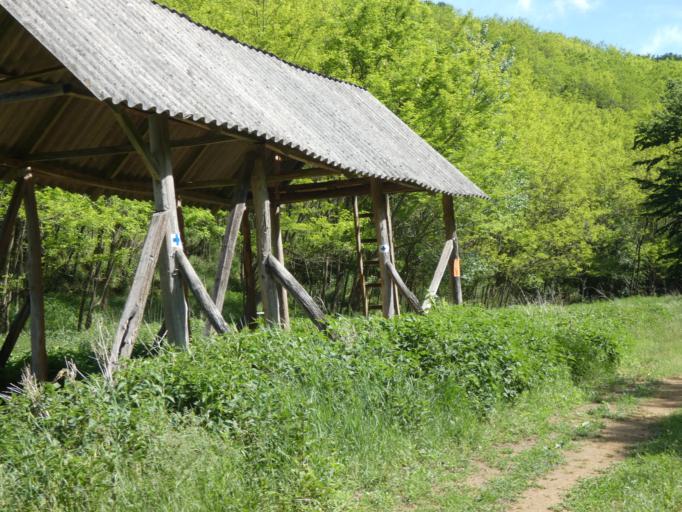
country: HU
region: Heves
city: Petervasara
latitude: 48.0839
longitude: 20.0969
